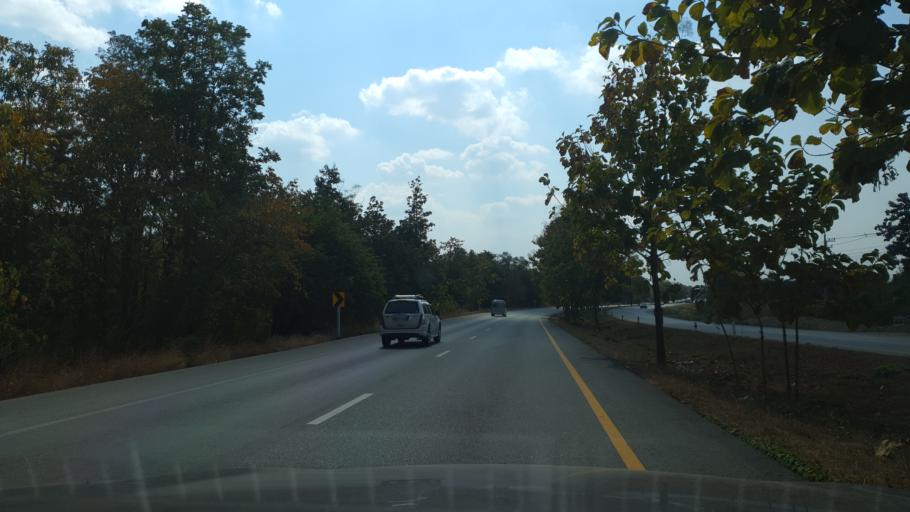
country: TH
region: Tak
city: Sam Ngao
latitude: 17.3047
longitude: 99.1477
